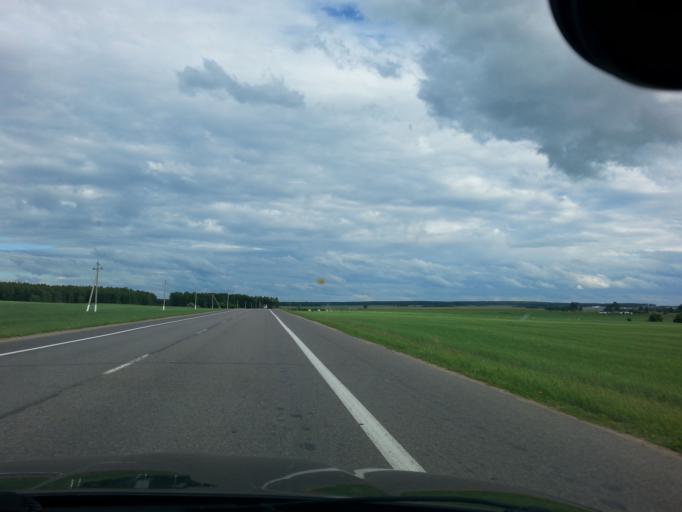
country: BY
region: Grodnenskaya
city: Astravyets
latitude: 54.7470
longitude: 26.0821
